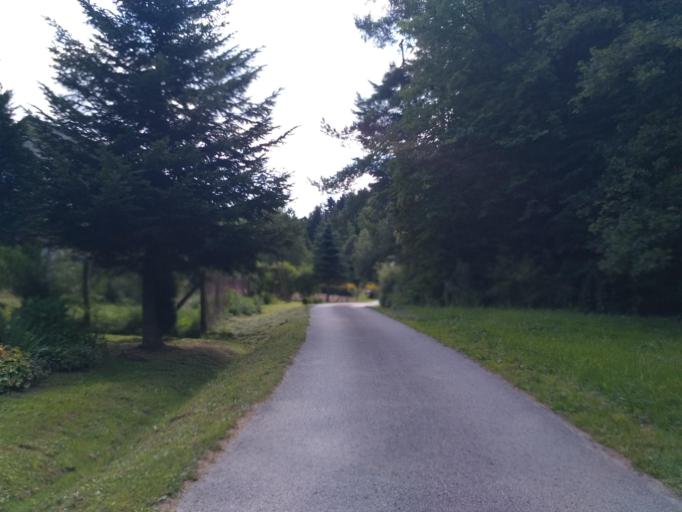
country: PL
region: Subcarpathian Voivodeship
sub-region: Powiat strzyzowski
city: Polomia
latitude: 49.9130
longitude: 21.8862
